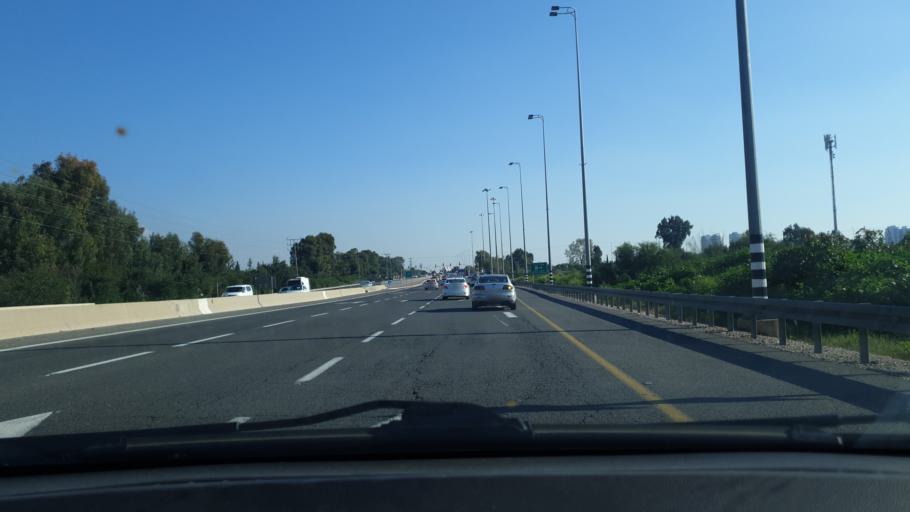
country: IL
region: Central District
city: Ramla
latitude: 31.9547
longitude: 34.8549
